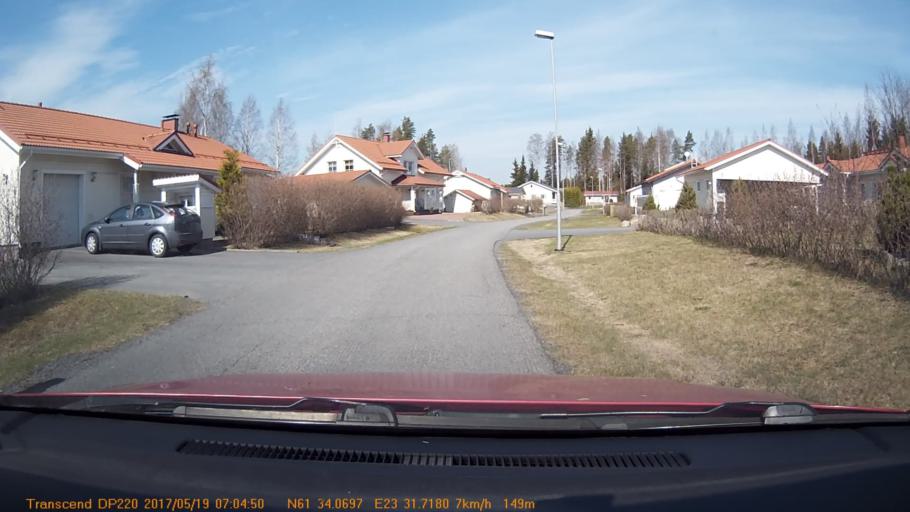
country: FI
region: Pirkanmaa
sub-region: Tampere
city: Yloejaervi
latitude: 61.5678
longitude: 23.5286
